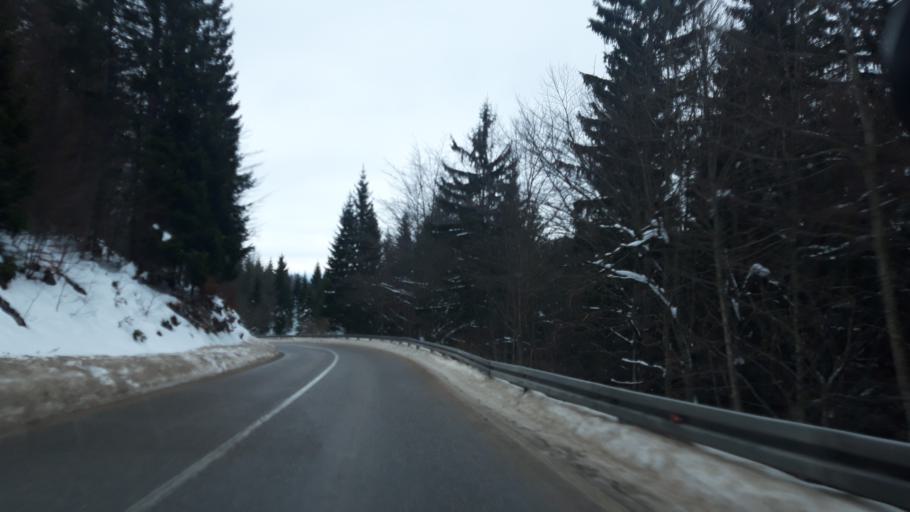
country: BA
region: Republika Srpska
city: Vlasenica
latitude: 44.1343
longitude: 18.9547
